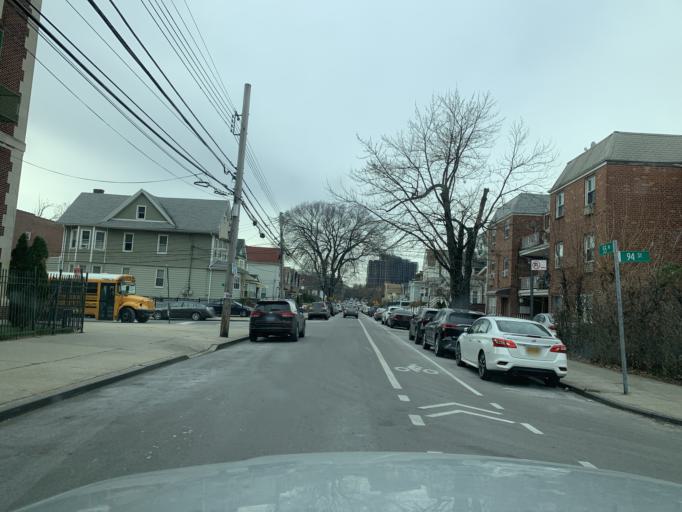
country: US
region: New York
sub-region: Queens County
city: Borough of Queens
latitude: 40.7378
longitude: -73.8682
